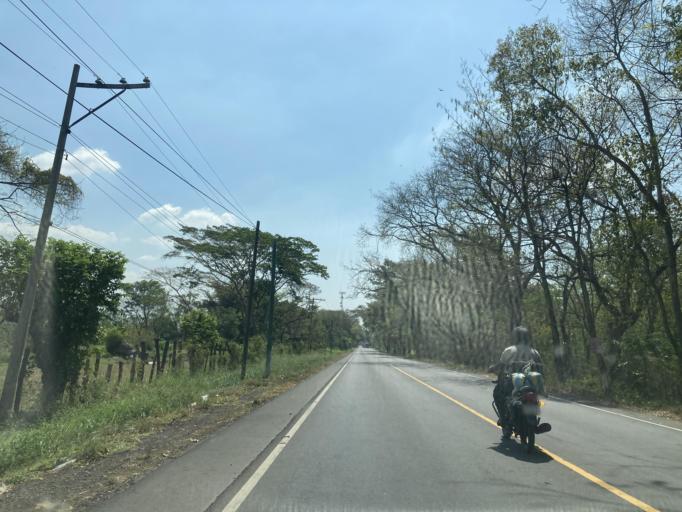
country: GT
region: Escuintla
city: Guanagazapa
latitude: 14.2109
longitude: -90.7215
